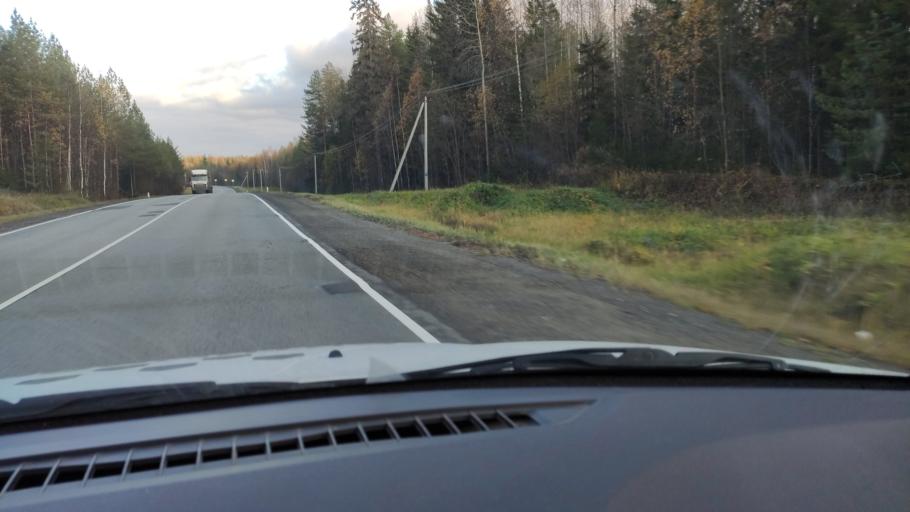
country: RU
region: Kirov
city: Belaya Kholunitsa
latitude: 58.9058
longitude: 51.0279
